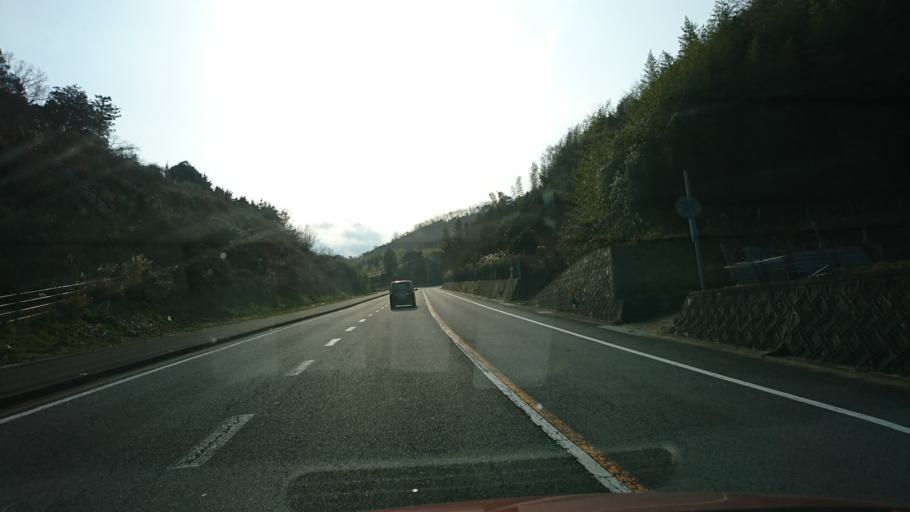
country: JP
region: Ehime
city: Hojo
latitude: 33.9978
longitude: 132.9347
